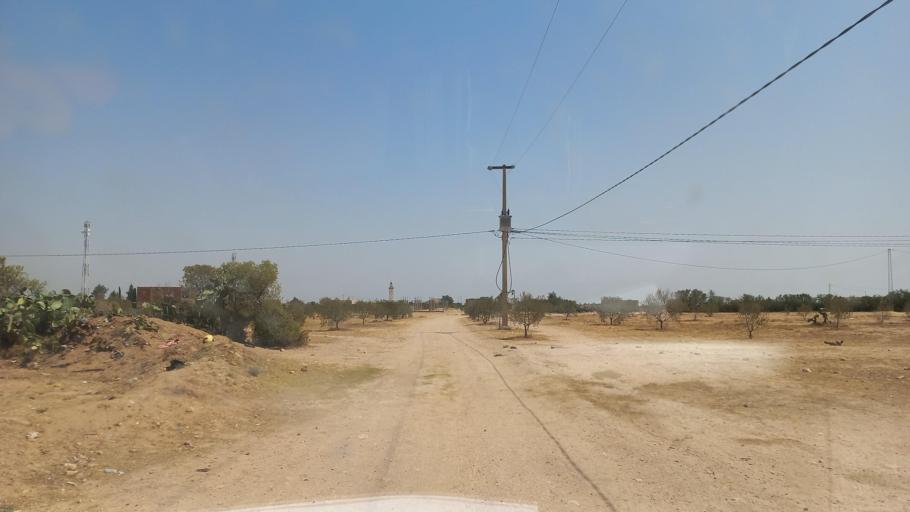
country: TN
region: Al Qasrayn
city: Kasserine
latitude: 35.2538
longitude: 9.0207
